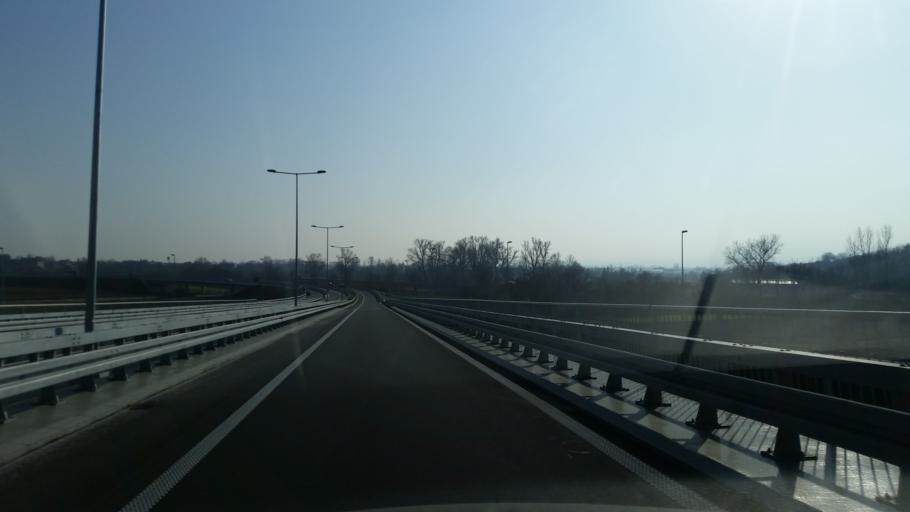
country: RS
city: Prislonica
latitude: 43.9199
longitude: 20.3940
